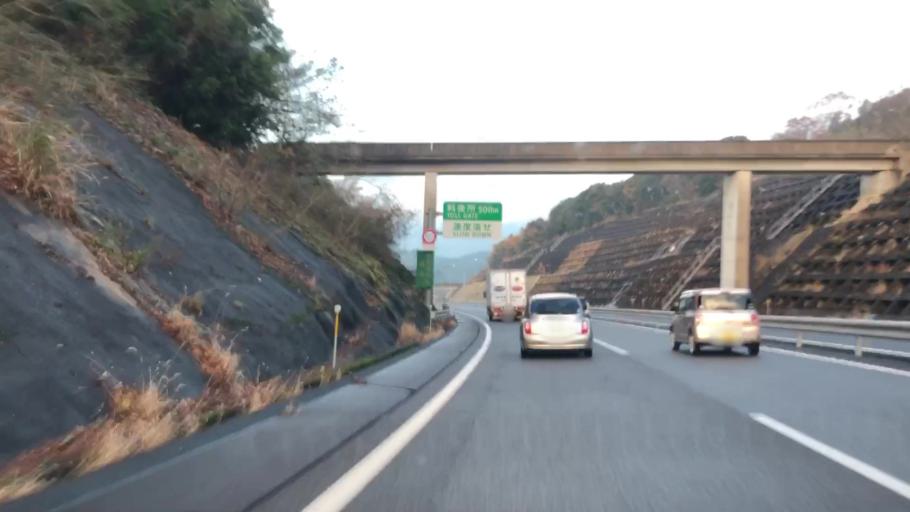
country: JP
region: Saga Prefecture
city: Imaricho-ko
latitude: 33.1687
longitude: 129.8539
